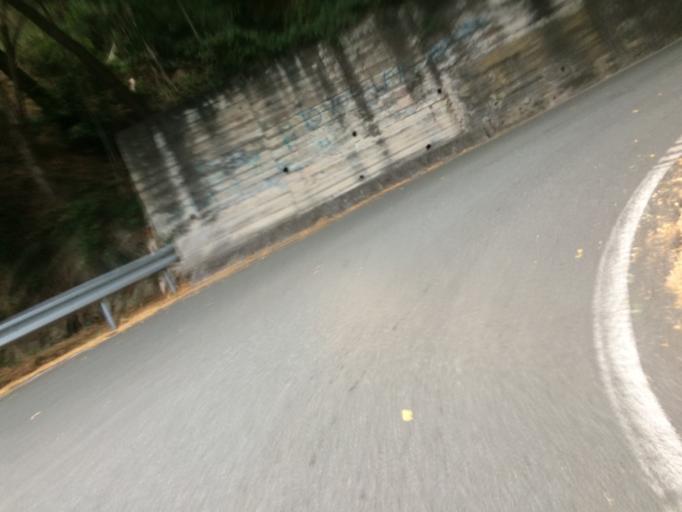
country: IT
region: Liguria
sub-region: Provincia di Imperia
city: Seborga
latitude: 43.8471
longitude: 7.7370
